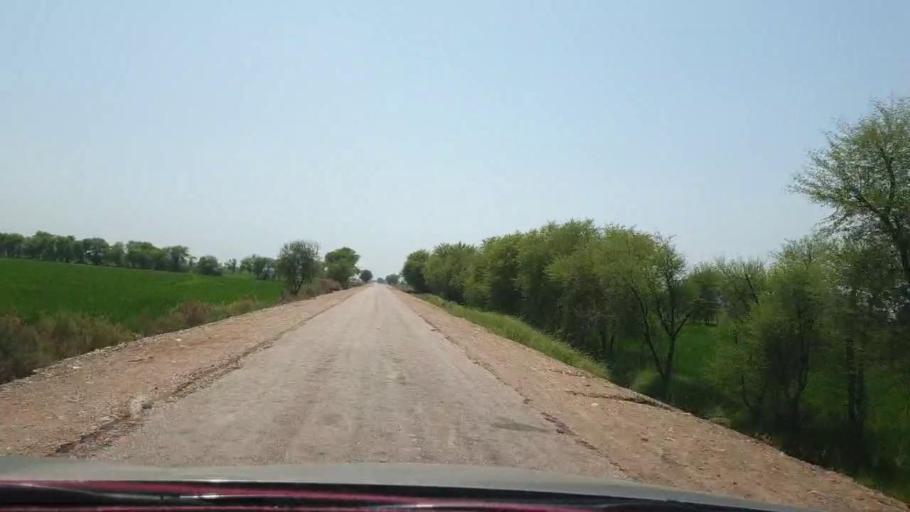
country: PK
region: Sindh
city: Warah
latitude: 27.5386
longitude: 67.7906
